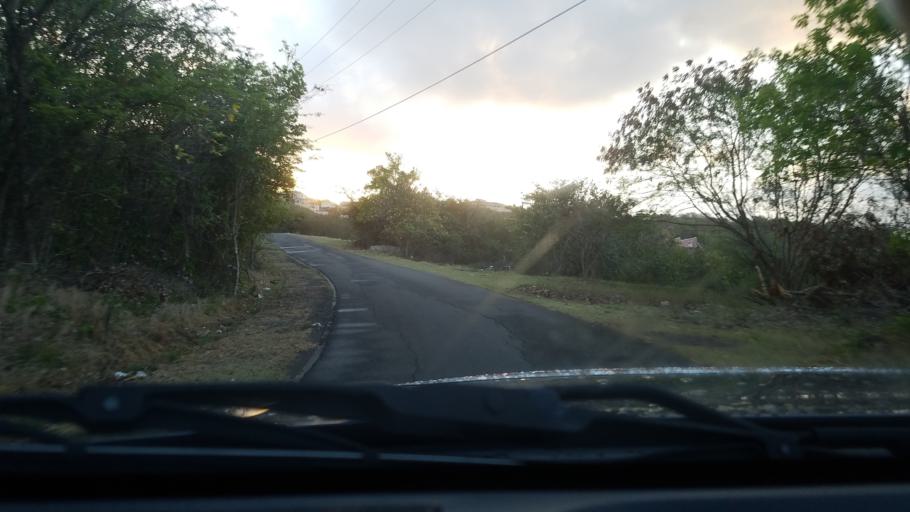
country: LC
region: Gros-Islet
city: Gros Islet
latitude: 14.0901
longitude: -60.9365
